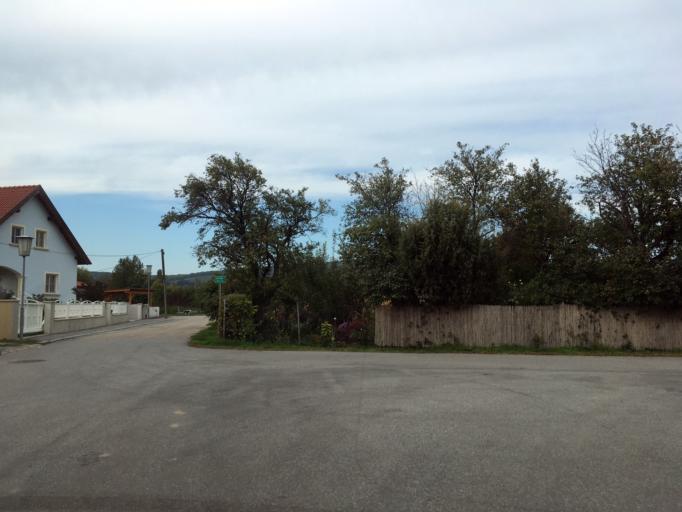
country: AT
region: Burgenland
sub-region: Politischer Bezirk Neusiedl am See
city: Winden am See
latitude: 47.9556
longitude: 16.7516
